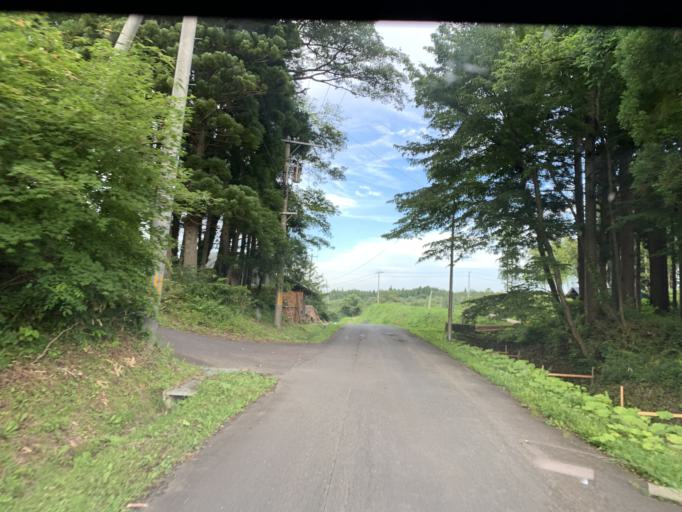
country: JP
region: Iwate
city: Ichinoseki
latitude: 38.9133
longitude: 141.0114
